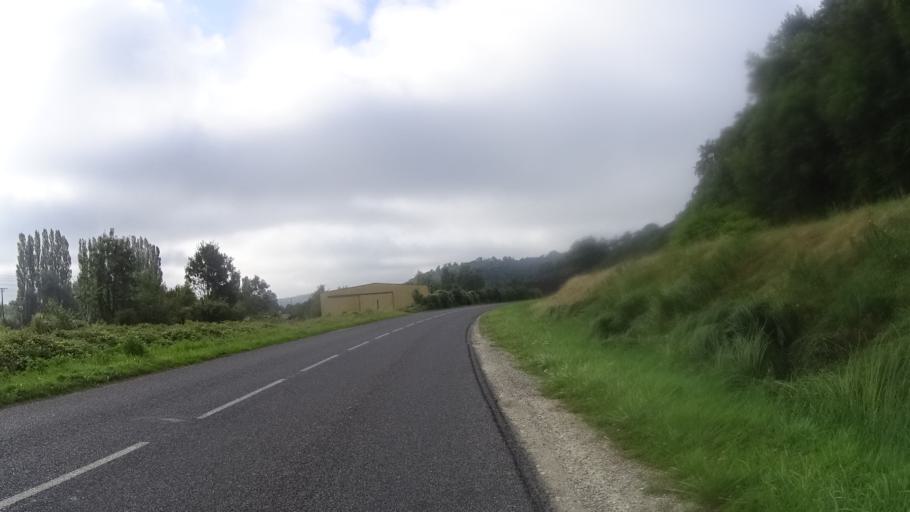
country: FR
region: Lorraine
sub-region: Departement de la Meuse
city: Fains-Veel
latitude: 48.8000
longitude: 5.1117
